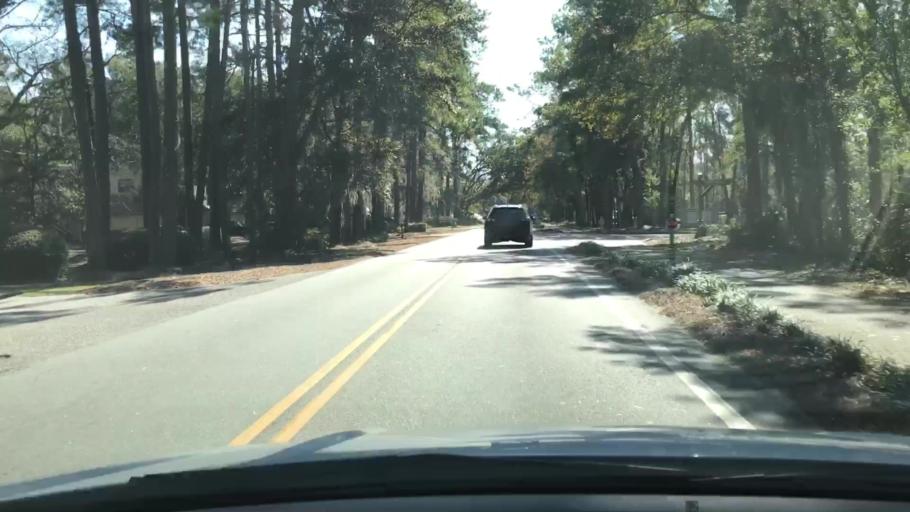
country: US
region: South Carolina
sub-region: Beaufort County
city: Hilton Head Island
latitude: 32.2205
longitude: -80.7047
